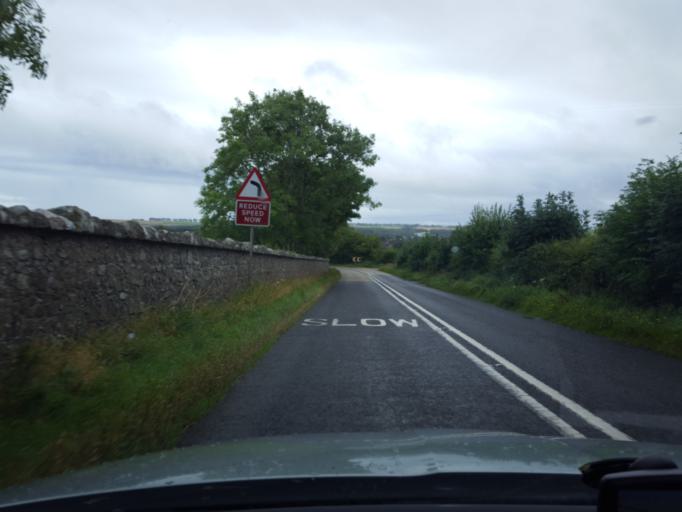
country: GB
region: Scotland
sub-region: Aberdeenshire
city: Stonehaven
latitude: 56.9776
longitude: -2.2427
